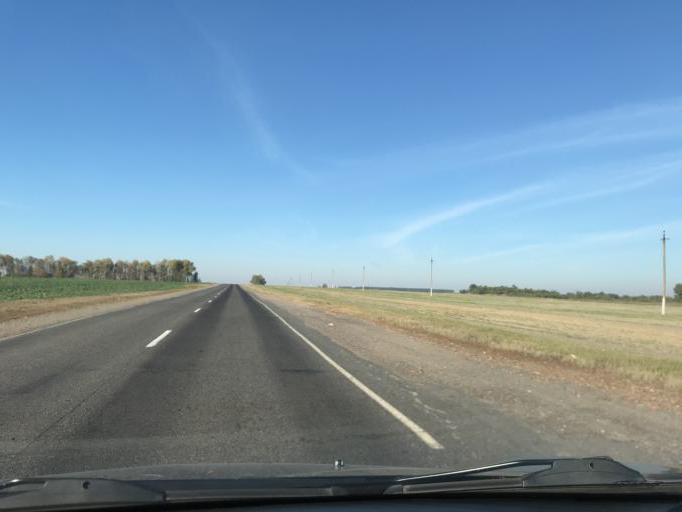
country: BY
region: Gomel
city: Brahin
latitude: 51.7974
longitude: 30.1432
